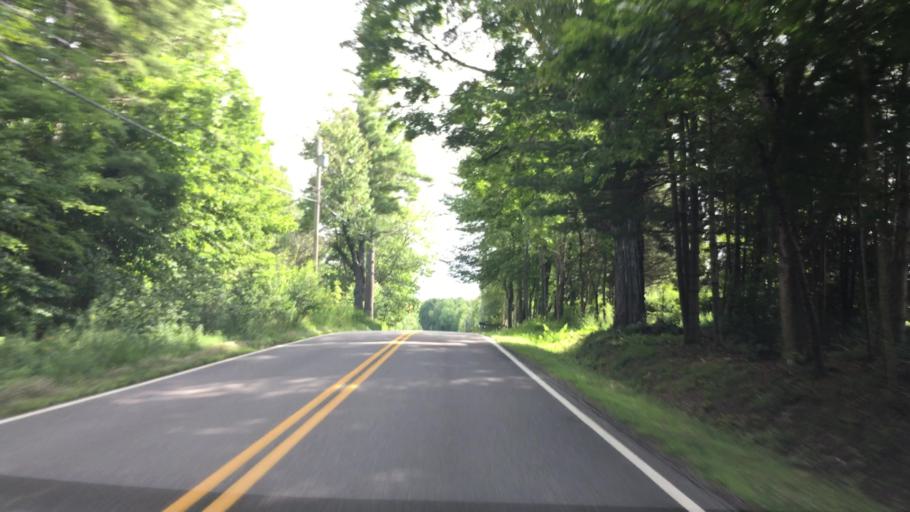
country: US
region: Maine
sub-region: Waldo County
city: Belfast
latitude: 44.3856
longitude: -69.0340
